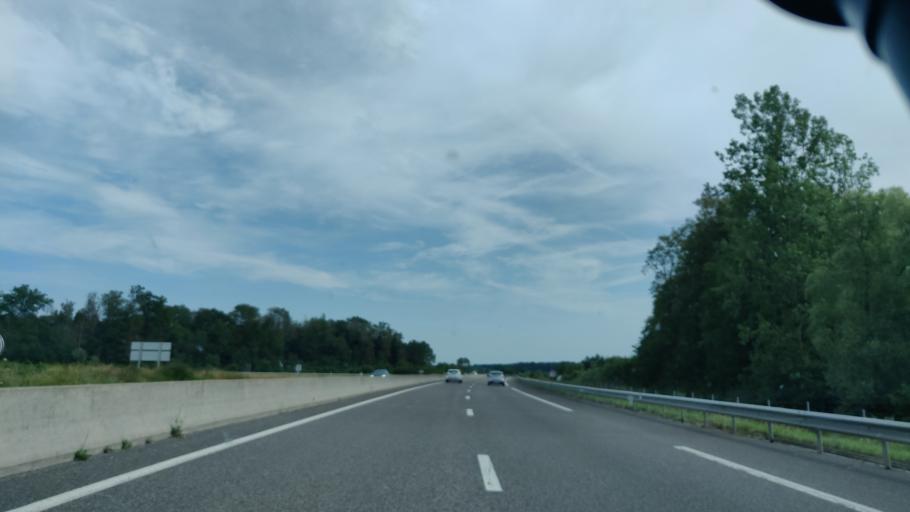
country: FR
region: Lorraine
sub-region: Departement de Meurthe-et-Moselle
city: Chanteheux
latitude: 48.5392
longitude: 6.5750
